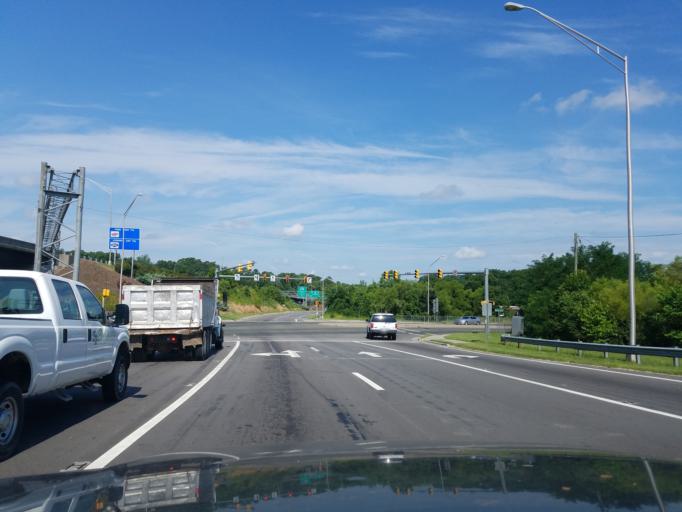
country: US
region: North Carolina
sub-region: Durham County
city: Durham
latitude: 36.0147
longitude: -78.8872
